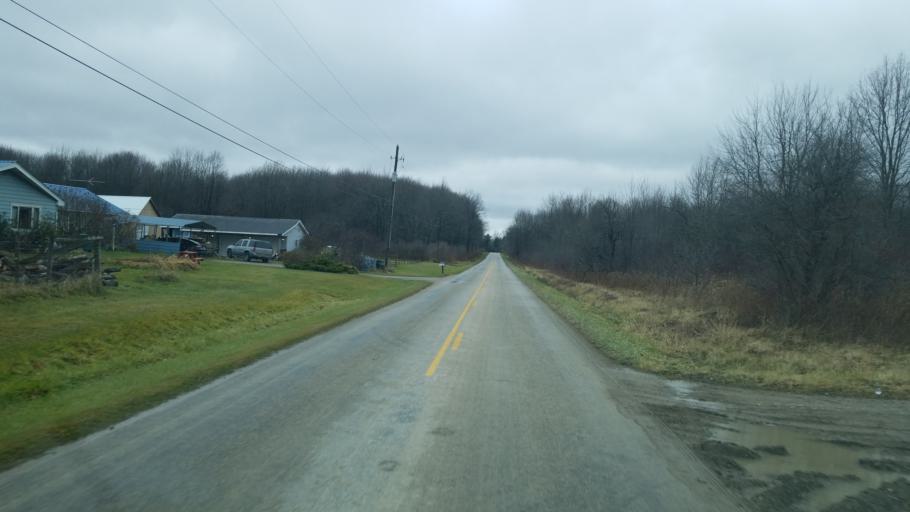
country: US
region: Ohio
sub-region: Ashtabula County
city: North Kingsville
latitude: 41.8090
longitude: -80.6243
